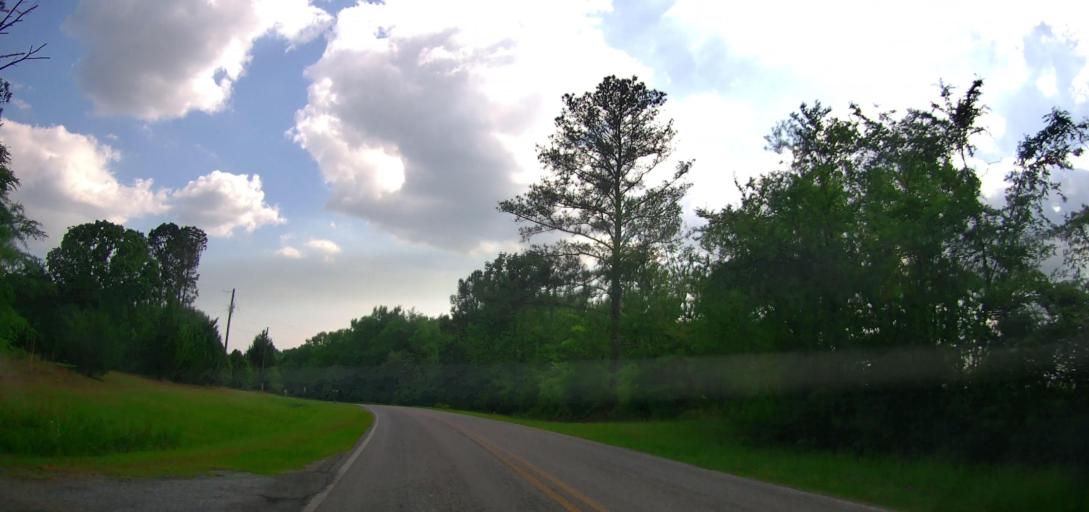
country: US
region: Georgia
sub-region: Laurens County
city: East Dublin
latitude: 32.6643
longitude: -82.8955
